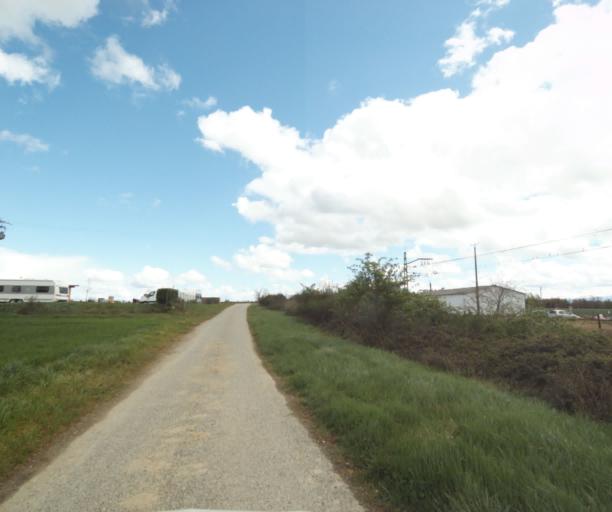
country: FR
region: Midi-Pyrenees
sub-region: Departement de l'Ariege
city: Saverdun
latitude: 43.2334
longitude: 1.5945
